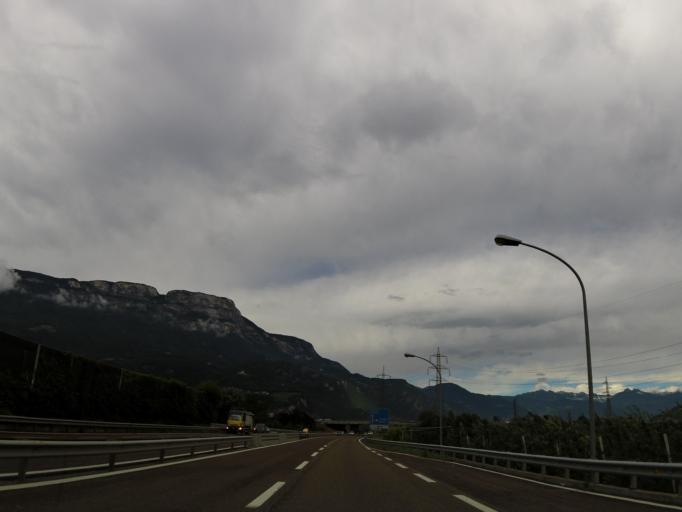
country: IT
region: Trentino-Alto Adige
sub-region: Bolzano
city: Cornaiano
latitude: 46.4849
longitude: 11.2932
